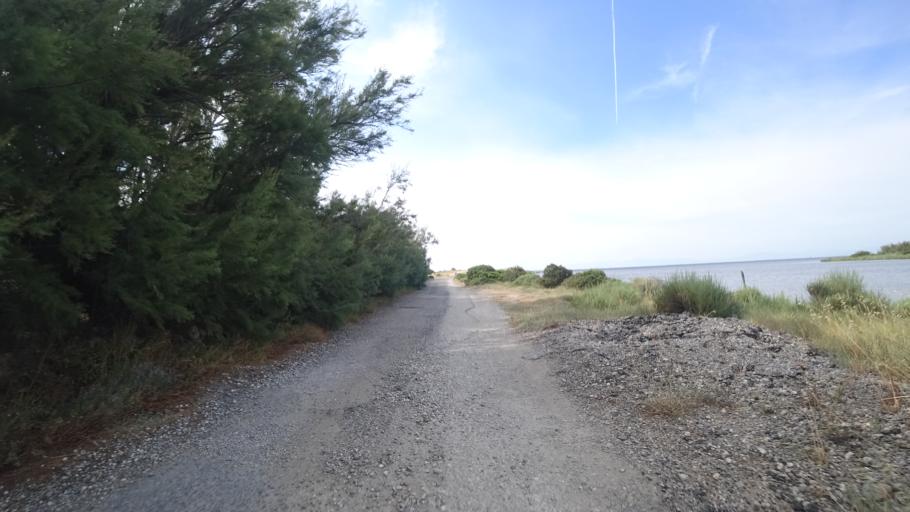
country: FR
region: Languedoc-Roussillon
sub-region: Departement de l'Aude
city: Leucate
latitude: 42.8976
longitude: 3.0283
